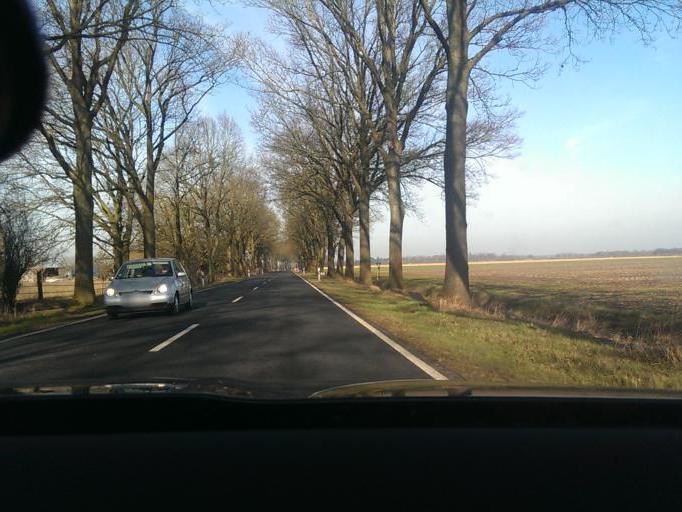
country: DE
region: Lower Saxony
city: Essel
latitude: 52.6688
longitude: 9.6595
